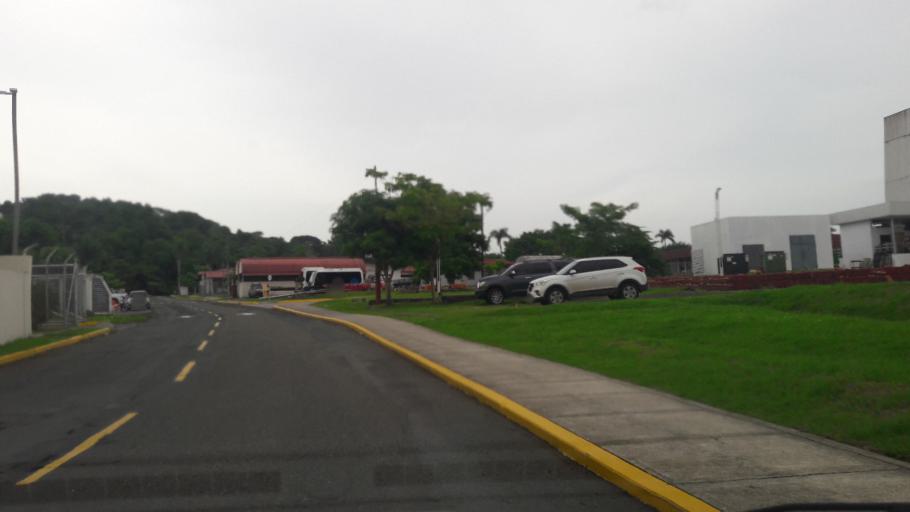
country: PA
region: Panama
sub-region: Distrito de Panama
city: Paraiso
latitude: 9.0020
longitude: -79.5854
